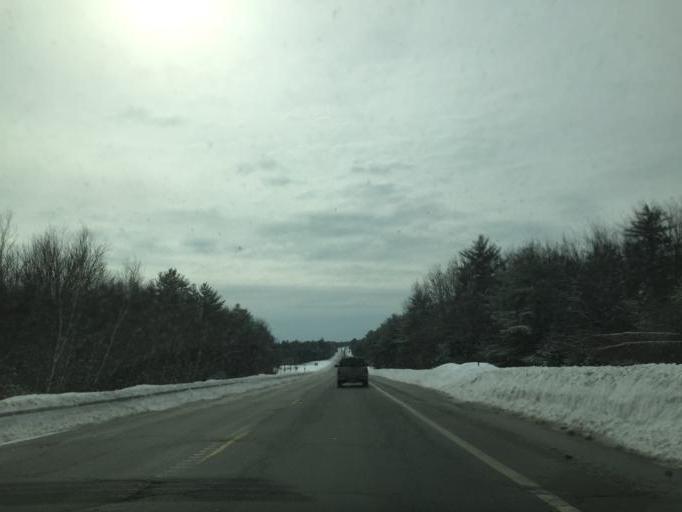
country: US
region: New Hampshire
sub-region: Strafford County
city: Rochester
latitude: 43.3534
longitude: -70.9860
